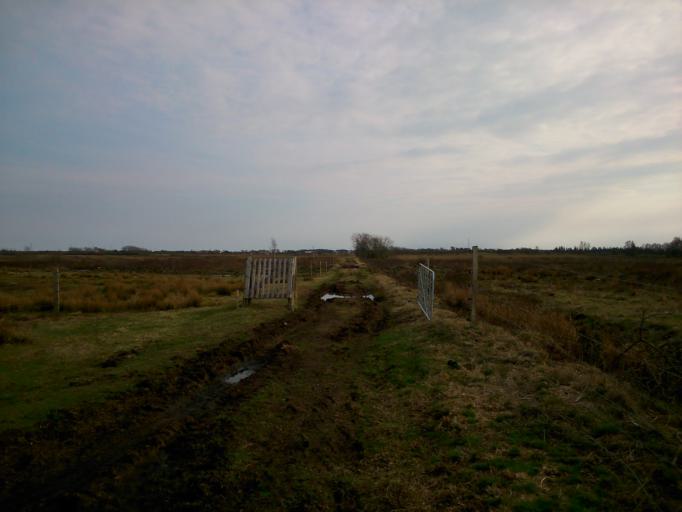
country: DK
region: South Denmark
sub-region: Tonder Kommune
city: Tonder
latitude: 55.0323
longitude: 8.8423
